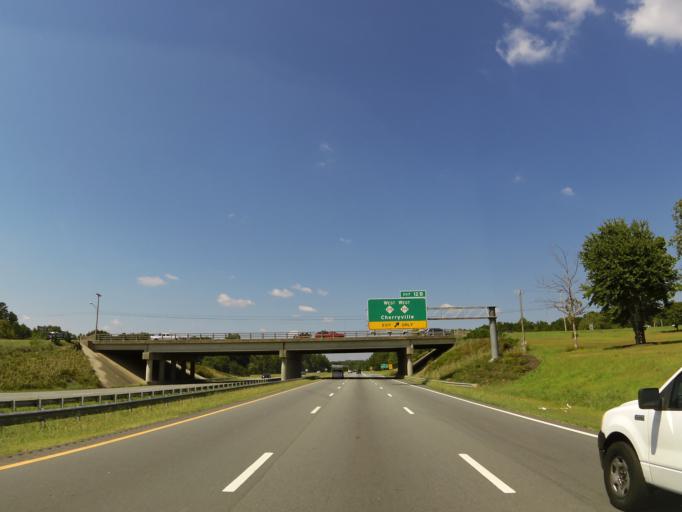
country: US
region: North Carolina
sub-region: Gaston County
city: Dallas
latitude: 35.3152
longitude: -81.1871
